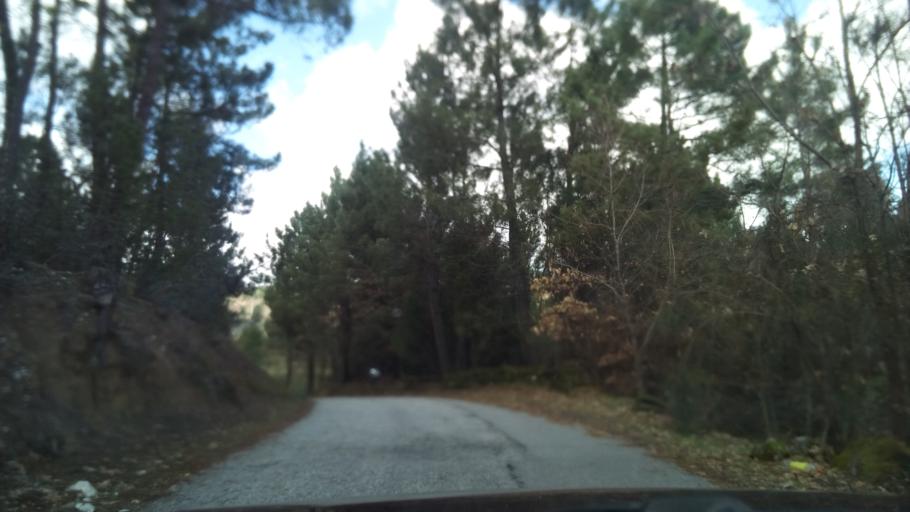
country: PT
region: Guarda
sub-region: Fornos de Algodres
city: Fornos de Algodres
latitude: 40.6280
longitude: -7.5252
